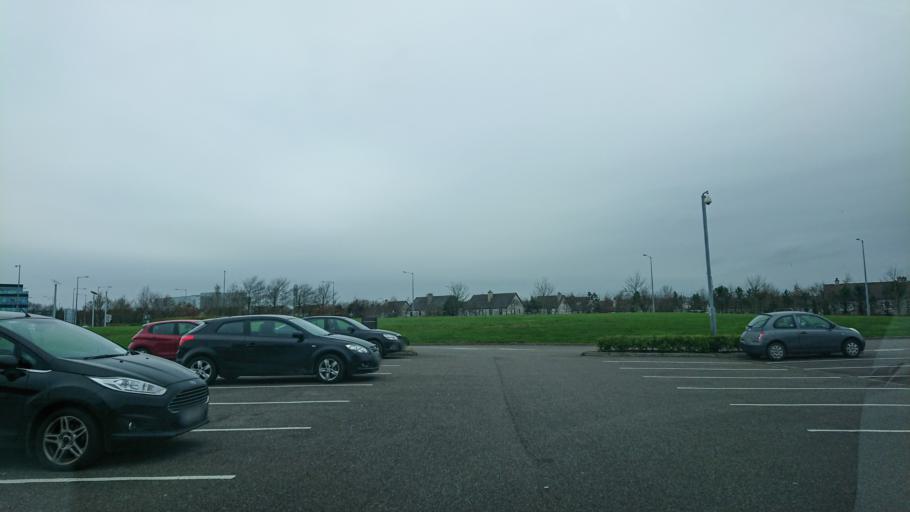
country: IE
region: Munster
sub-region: County Cork
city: Passage West
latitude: 51.8866
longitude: -8.3976
